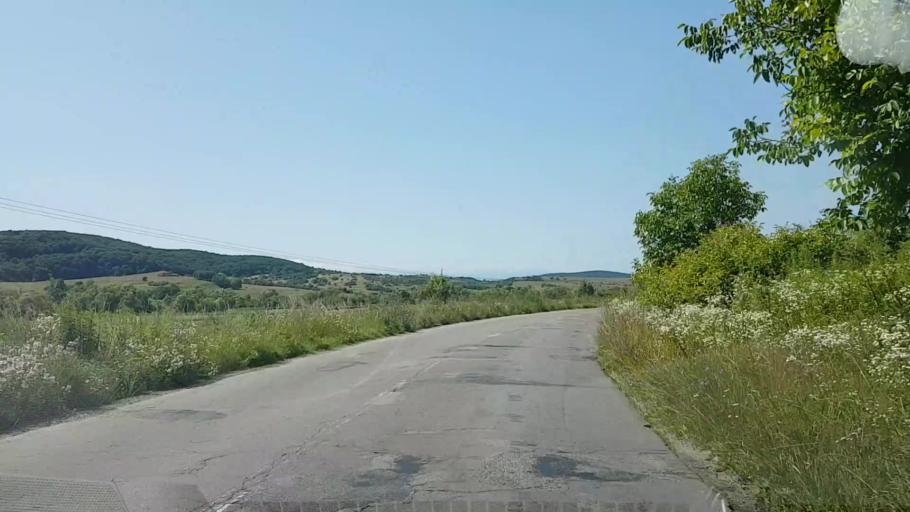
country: RO
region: Sibiu
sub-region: Comuna Iacobeni
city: Iacobeni
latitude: 46.0323
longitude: 24.7171
